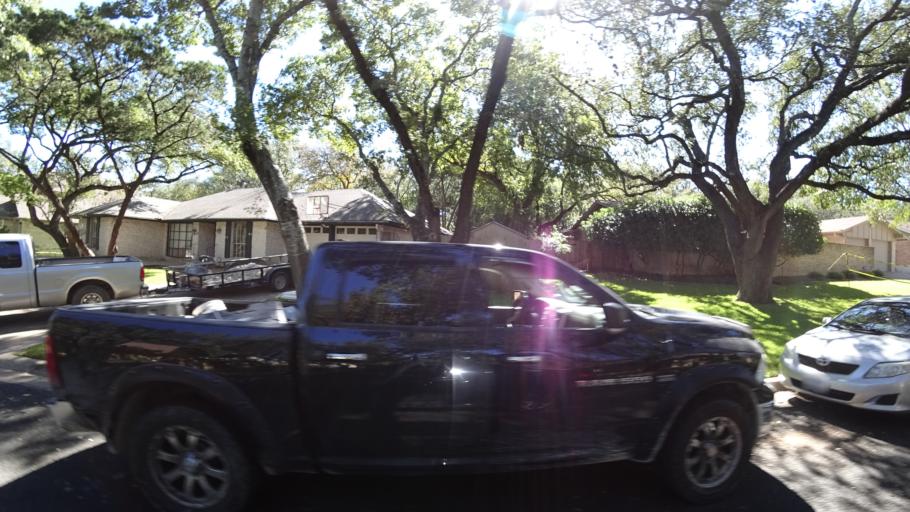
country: US
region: Texas
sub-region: Travis County
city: West Lake Hills
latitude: 30.3604
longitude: -97.7608
